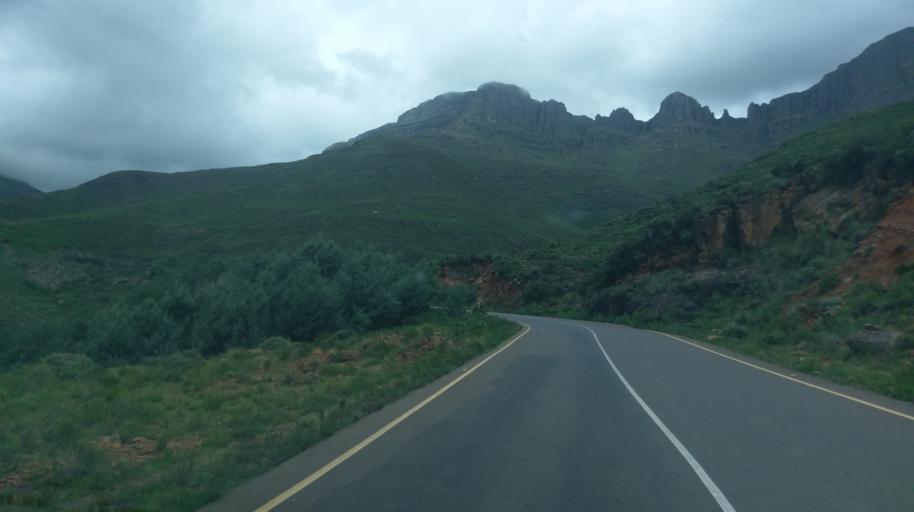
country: LS
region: Butha-Buthe
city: Butha-Buthe
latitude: -29.0578
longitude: 28.3547
